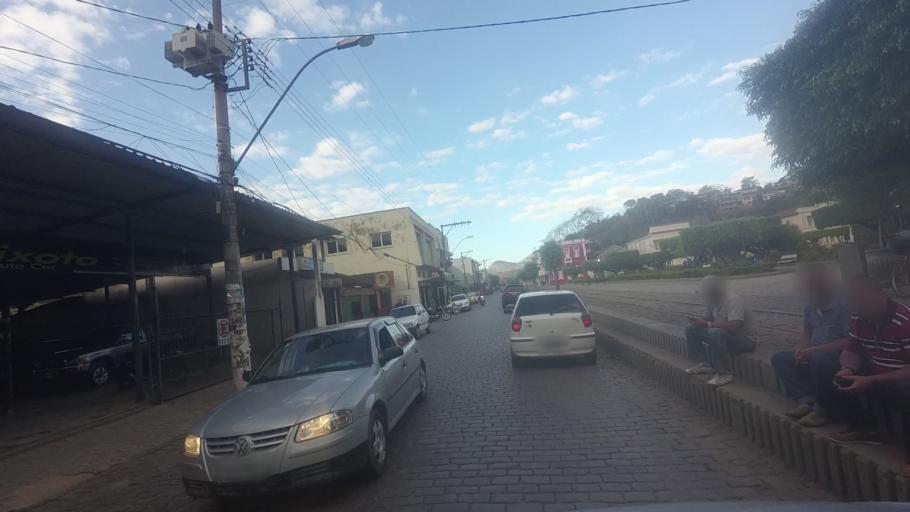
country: BR
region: Espirito Santo
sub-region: Mimoso Do Sul
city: Mimoso do Sul
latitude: -20.9509
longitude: -41.3451
